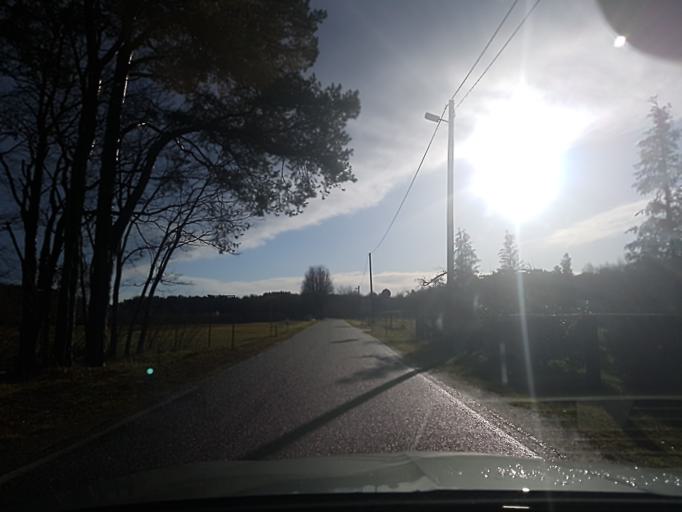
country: DE
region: Brandenburg
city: Falkenberg
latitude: 51.5927
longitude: 13.3115
